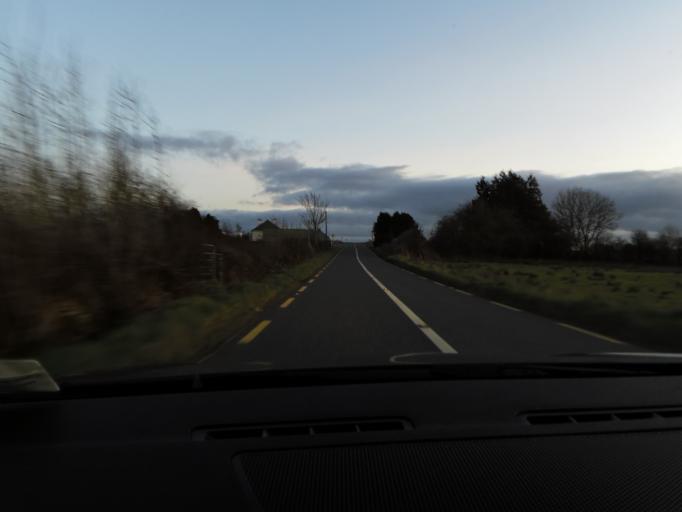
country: IE
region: Connaught
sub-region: Roscommon
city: Boyle
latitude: 53.8760
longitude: -8.2485
